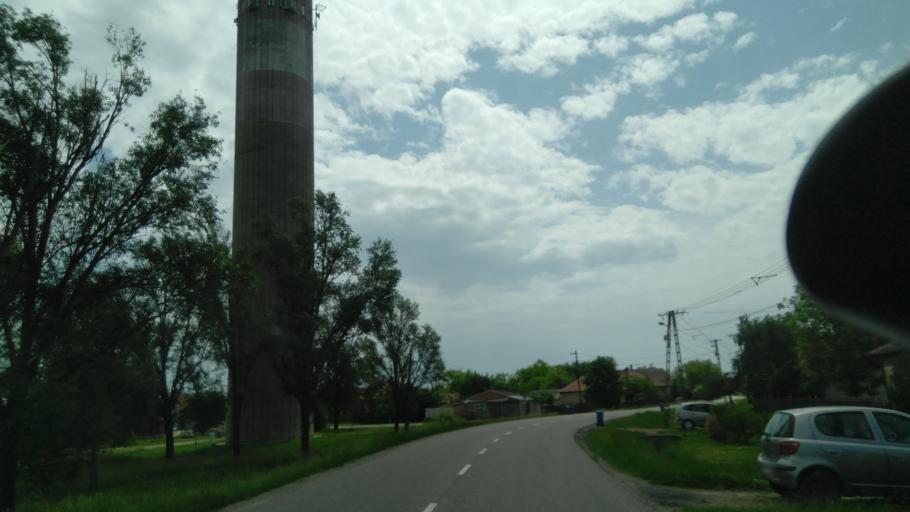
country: HU
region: Hajdu-Bihar
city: Komadi
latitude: 47.0135
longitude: 21.4983
